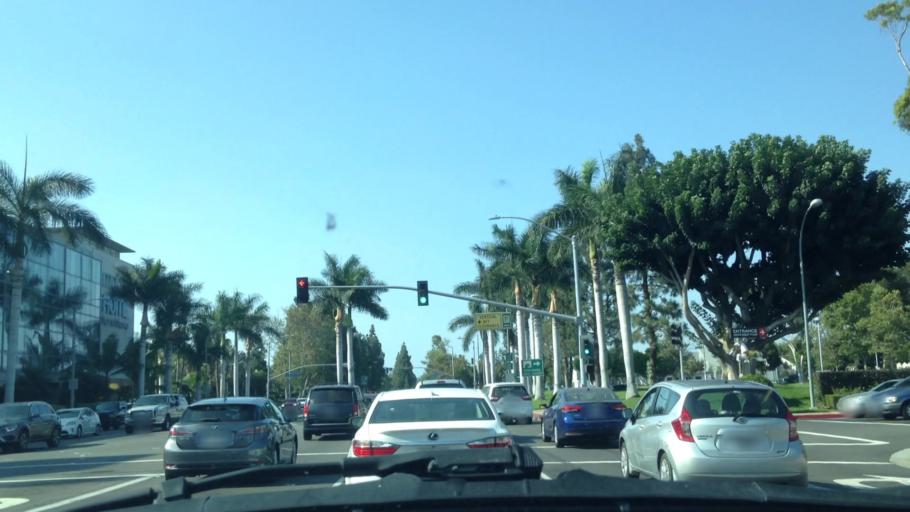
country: US
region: California
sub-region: Orange County
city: Costa Mesa
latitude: 33.6925
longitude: -117.8921
